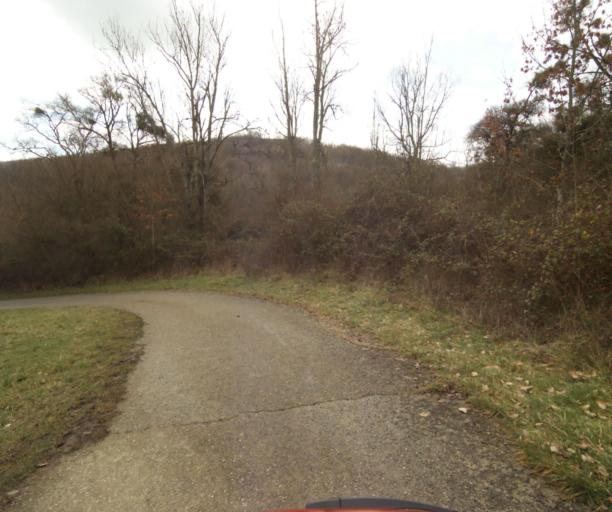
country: FR
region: Midi-Pyrenees
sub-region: Departement de l'Ariege
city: Pamiers
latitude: 43.1074
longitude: 1.6009
